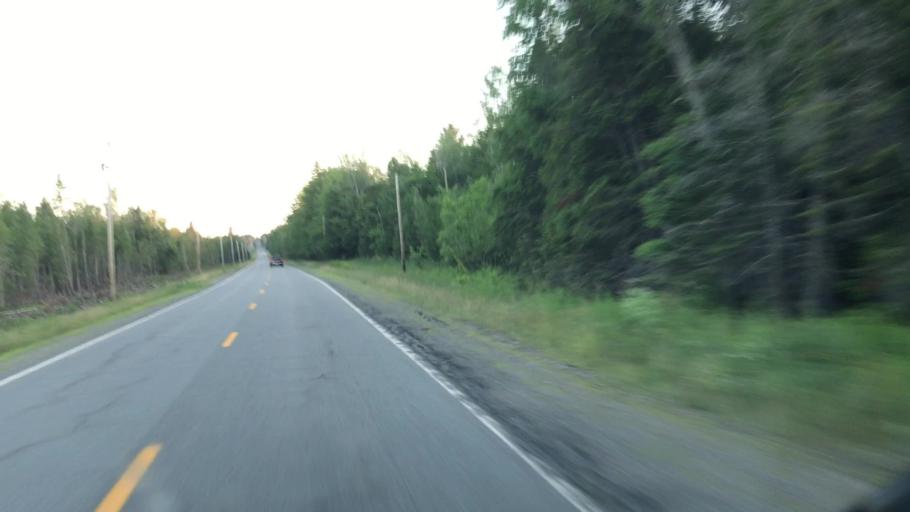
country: US
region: Maine
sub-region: Penobscot County
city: Medway
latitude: 45.6102
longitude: -68.3058
